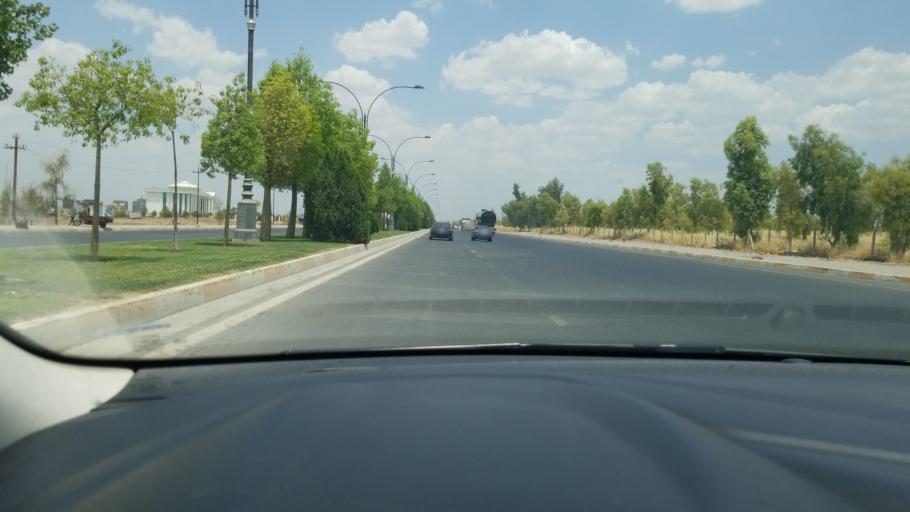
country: IQ
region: Arbil
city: Erbil
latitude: 36.1146
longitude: 44.0229
